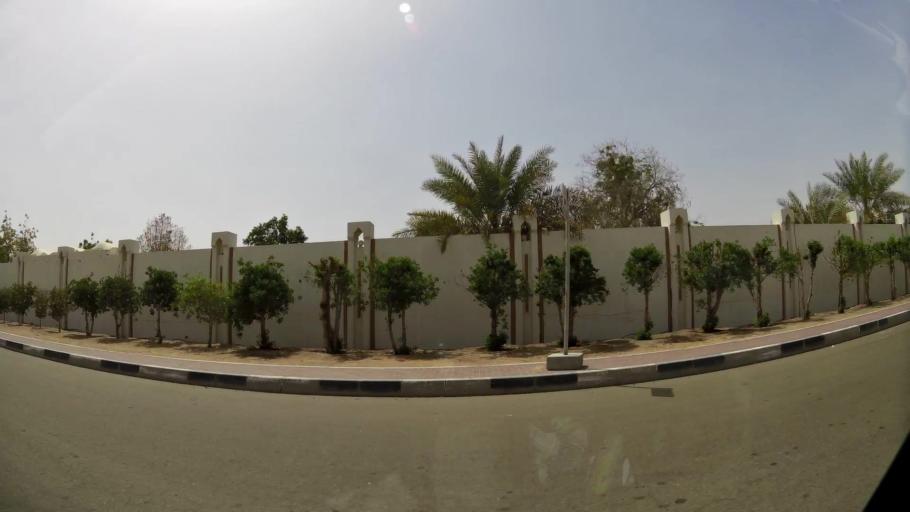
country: AE
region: Abu Dhabi
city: Al Ain
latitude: 24.1603
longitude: 55.6678
